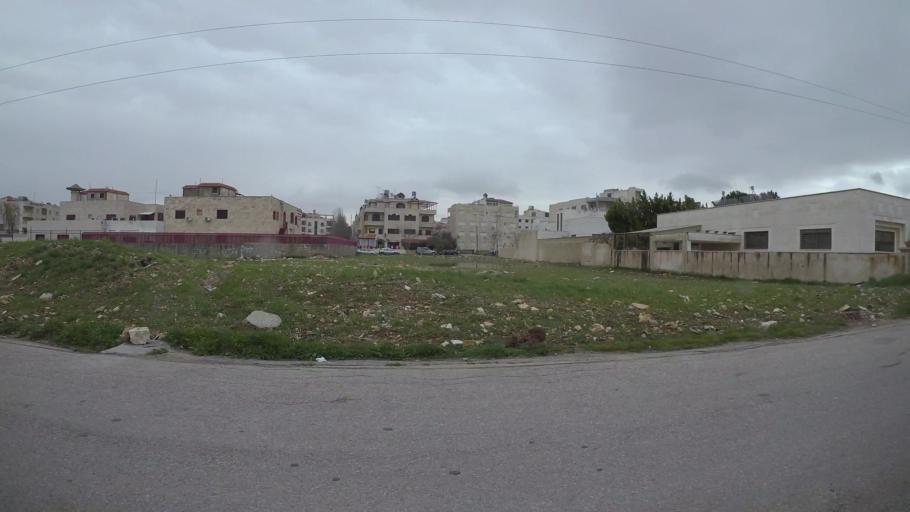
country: JO
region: Amman
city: Al Jubayhah
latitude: 31.9913
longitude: 35.8442
